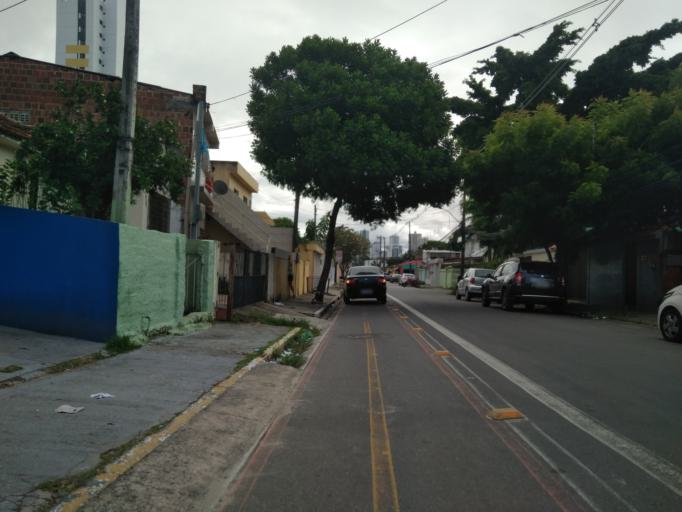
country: BR
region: Pernambuco
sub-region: Recife
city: Recife
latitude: -8.0308
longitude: -34.8820
